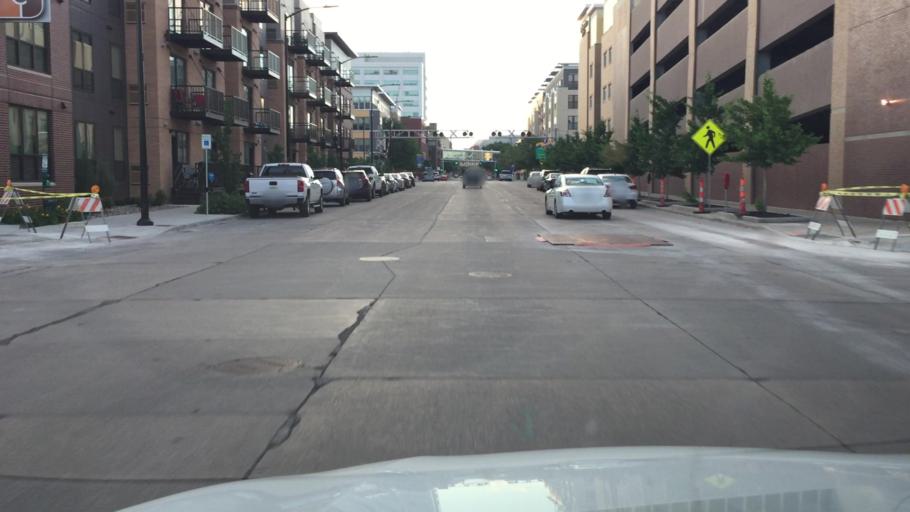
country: US
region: Iowa
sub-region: Polk County
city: Des Moines
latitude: 41.5832
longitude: -93.6184
